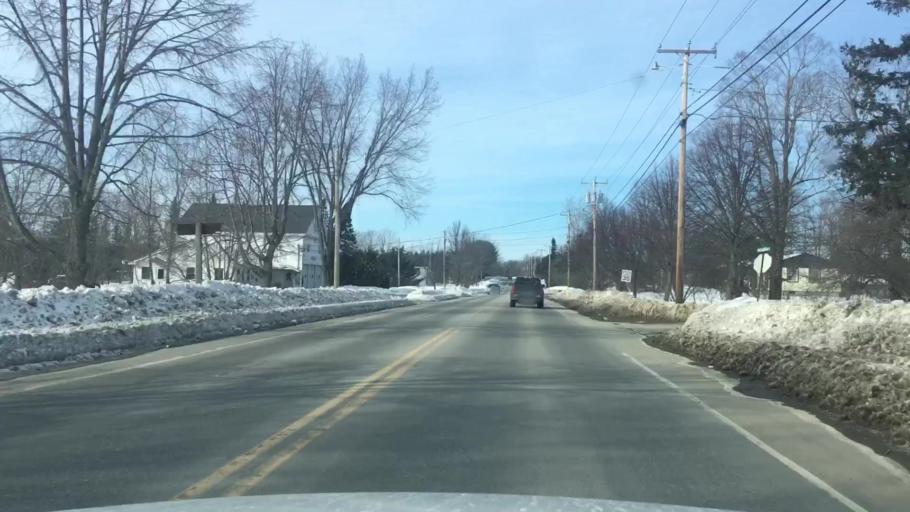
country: US
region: Maine
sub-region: Penobscot County
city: Kenduskeag
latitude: 44.9217
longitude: -68.9319
